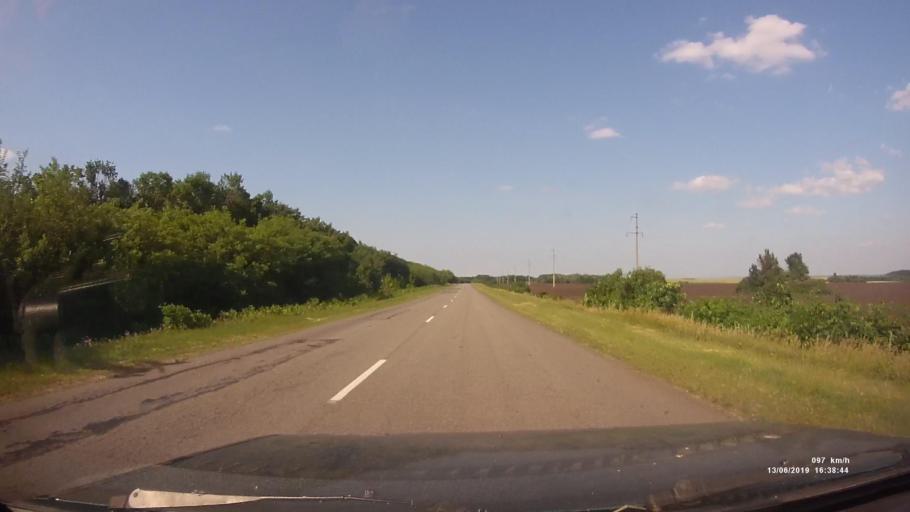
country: RU
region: Rostov
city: Kazanskaya
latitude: 49.9218
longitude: 41.3284
